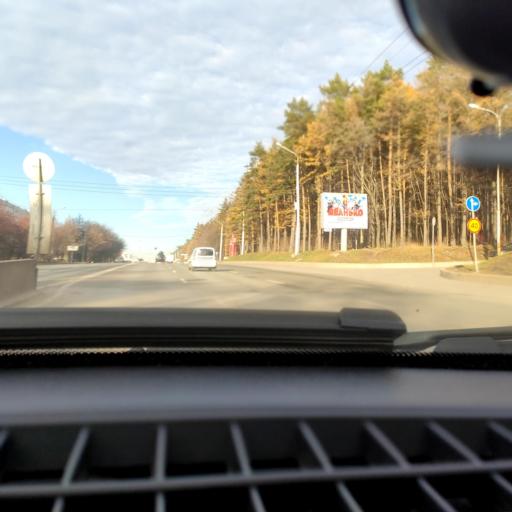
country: RU
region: Bashkortostan
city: Ufa
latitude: 54.7371
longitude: 56.0274
